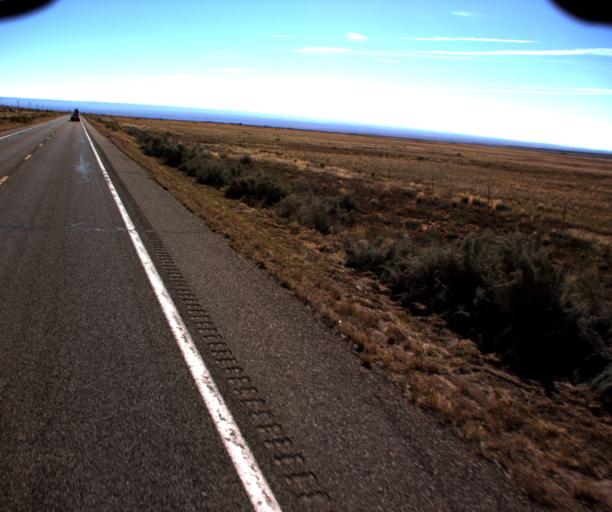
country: US
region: Arizona
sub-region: Mohave County
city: Colorado City
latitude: 36.8723
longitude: -112.8617
